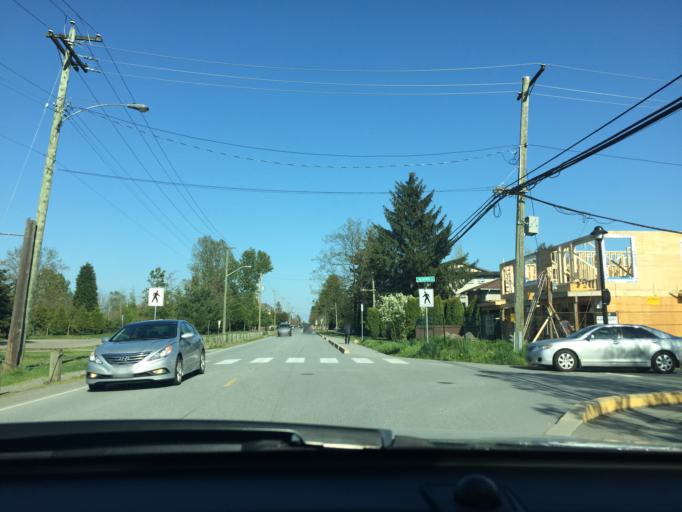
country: CA
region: British Columbia
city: Richmond
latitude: 49.1628
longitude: -123.1229
